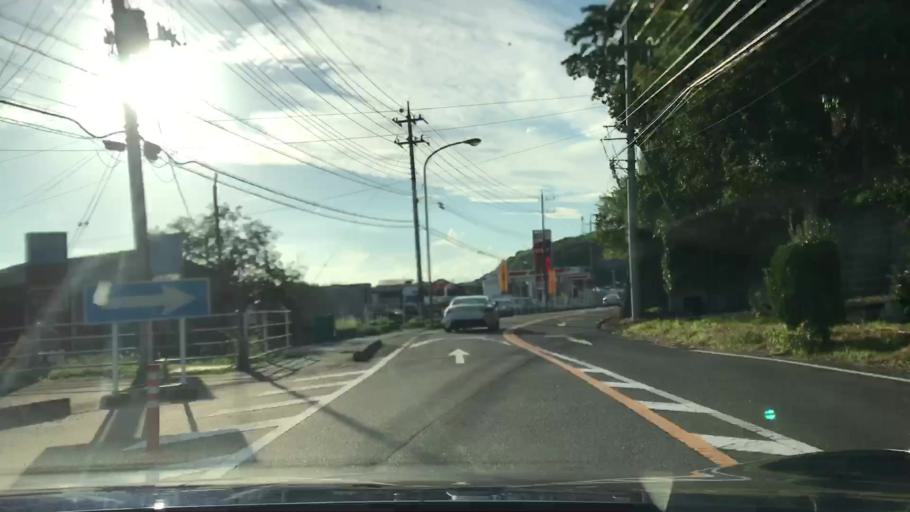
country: JP
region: Tochigi
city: Motegi
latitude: 36.5322
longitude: 140.2009
